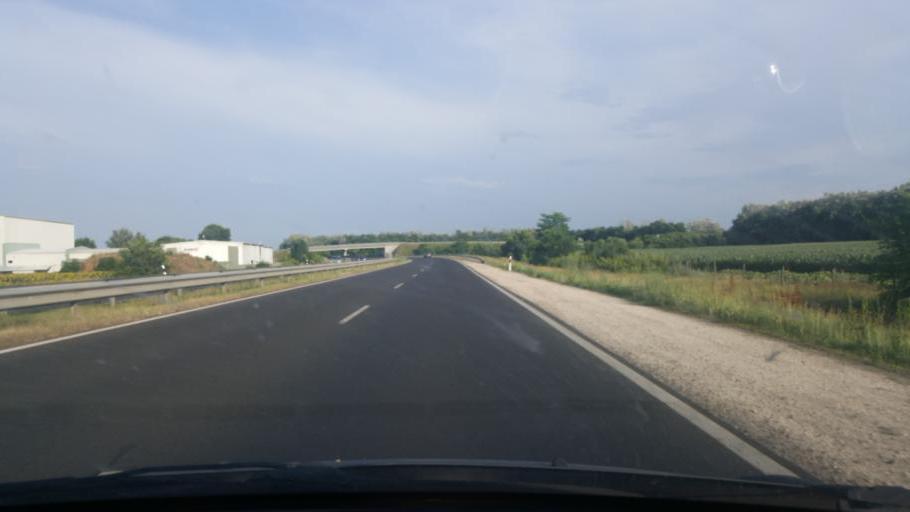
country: HU
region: Pest
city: Vecses
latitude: 47.4174
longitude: 19.2784
